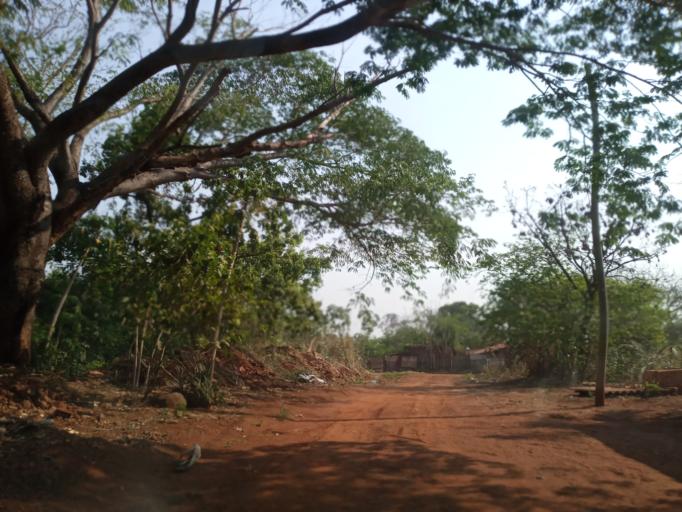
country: BR
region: Minas Gerais
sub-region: Ituiutaba
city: Ituiutaba
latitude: -18.9611
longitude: -49.4755
